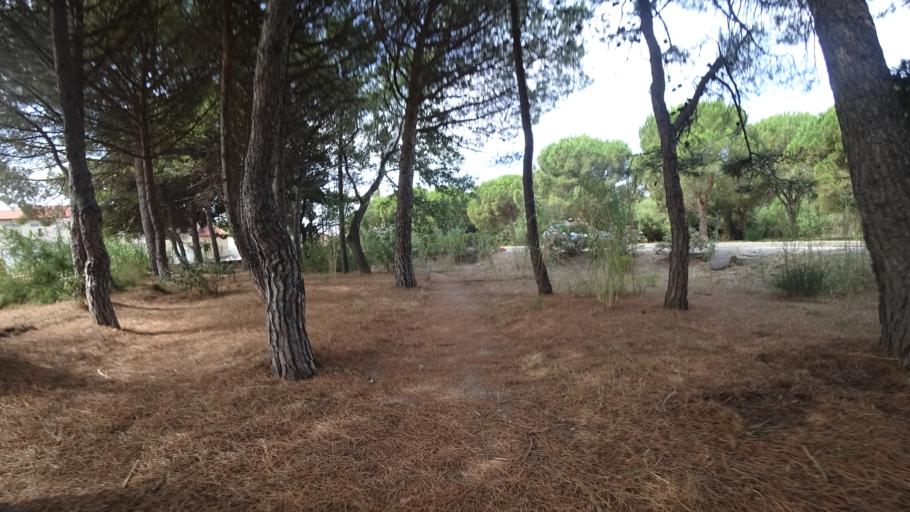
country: FR
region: Languedoc-Roussillon
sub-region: Departement de l'Aude
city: Leucate
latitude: 42.8509
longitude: 3.0371
